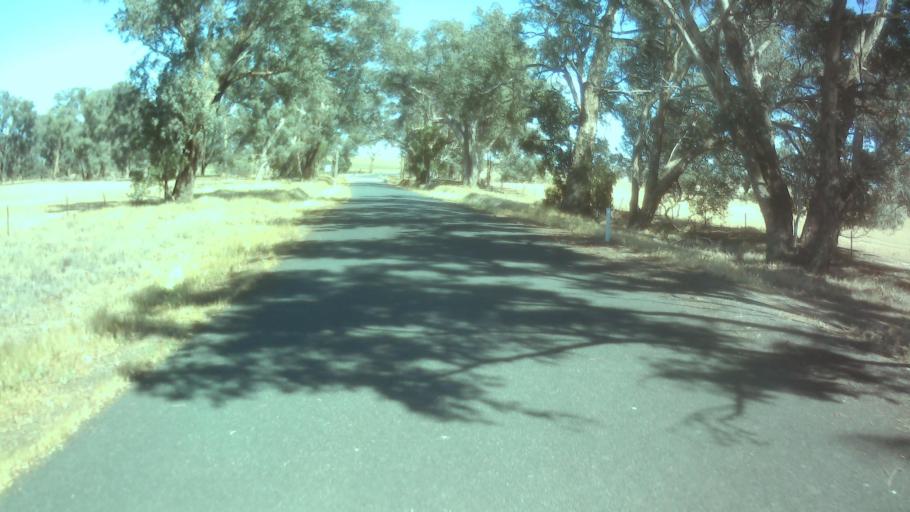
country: AU
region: New South Wales
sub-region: Weddin
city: Grenfell
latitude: -33.9854
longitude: 148.4091
